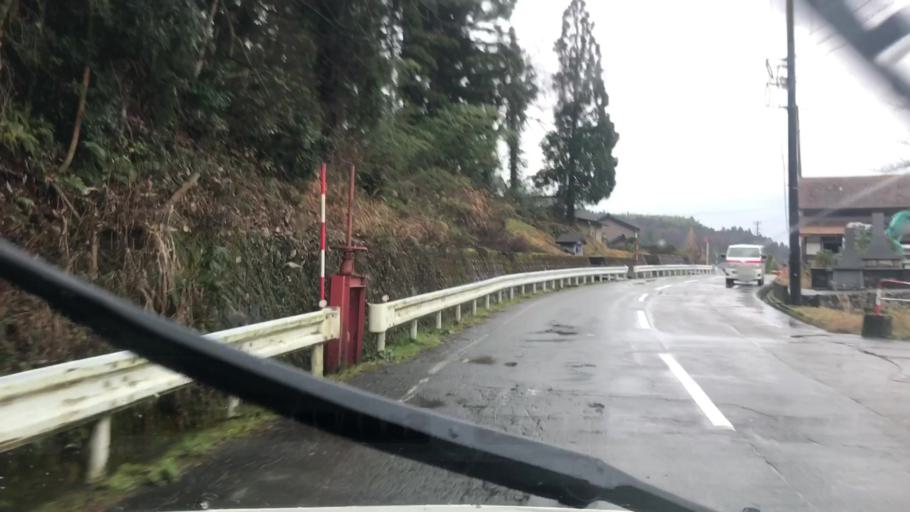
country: JP
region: Toyama
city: Toyama-shi
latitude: 36.6029
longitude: 137.2746
